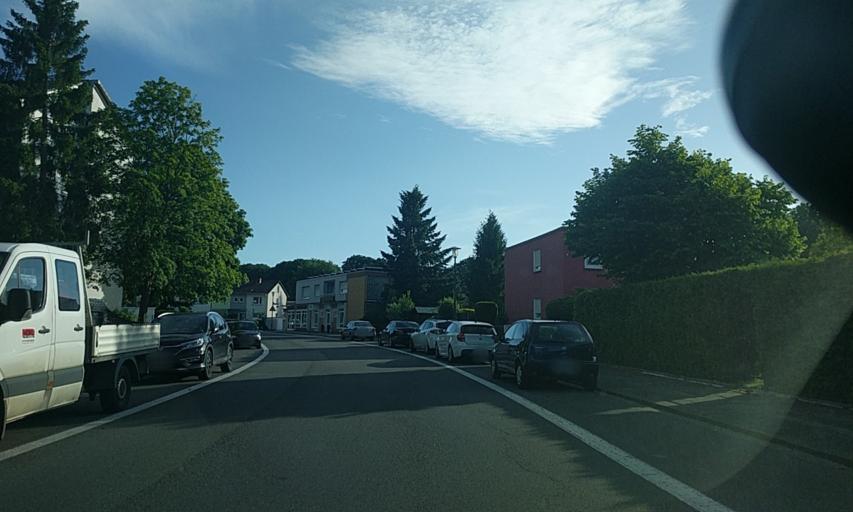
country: DE
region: Rheinland-Pfalz
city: Kaiserslautern
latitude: 49.4335
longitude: 7.7243
